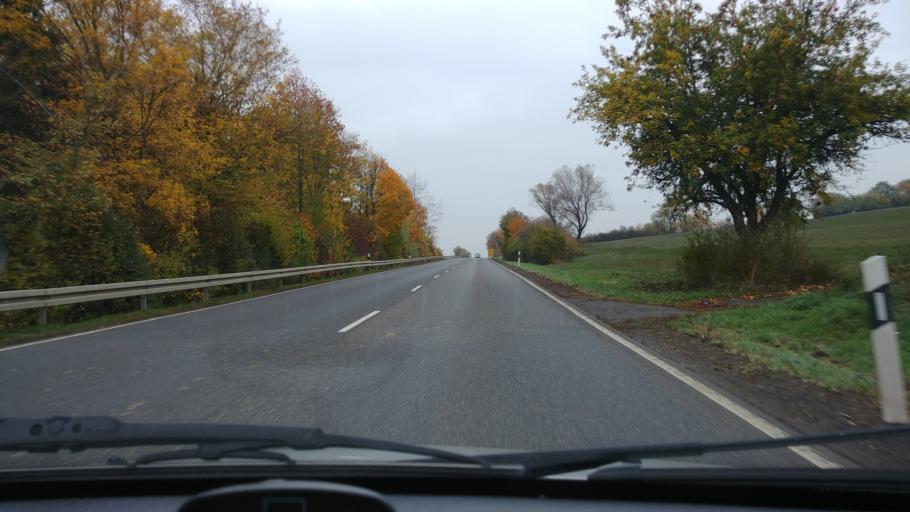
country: DE
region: Hesse
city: Waldbrunn
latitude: 50.4854
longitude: 8.0604
